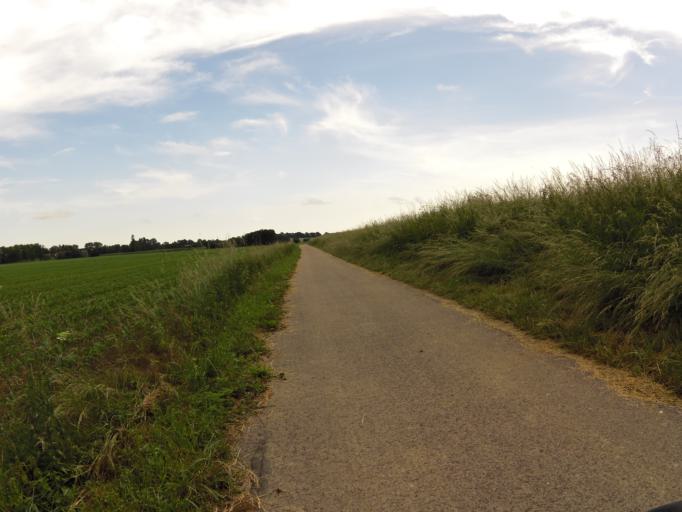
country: FR
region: Champagne-Ardenne
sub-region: Departement de l'Aube
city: Lusigny-sur-Barse
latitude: 48.2708
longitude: 4.2530
